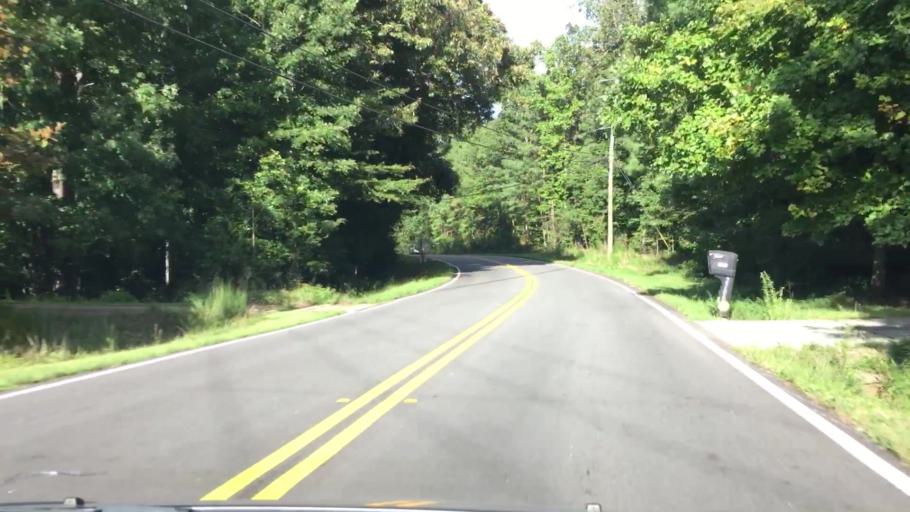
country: US
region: Georgia
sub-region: Henry County
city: Stockbridge
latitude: 33.5799
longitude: -84.1868
